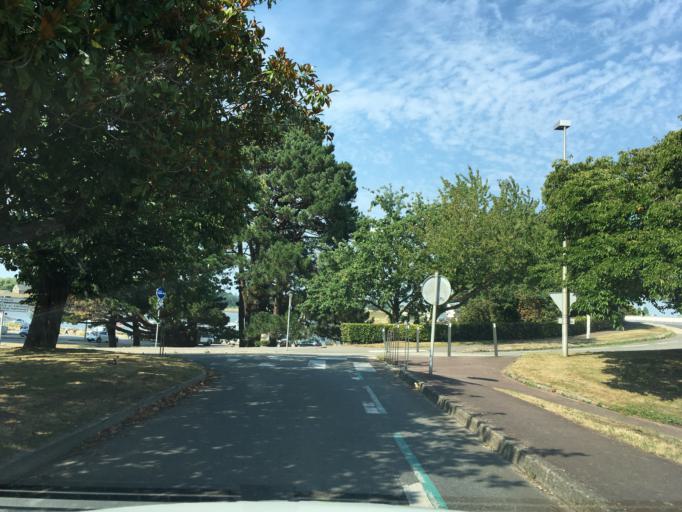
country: FR
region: Brittany
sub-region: Departement du Morbihan
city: Lorient
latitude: 47.7602
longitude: -3.3660
